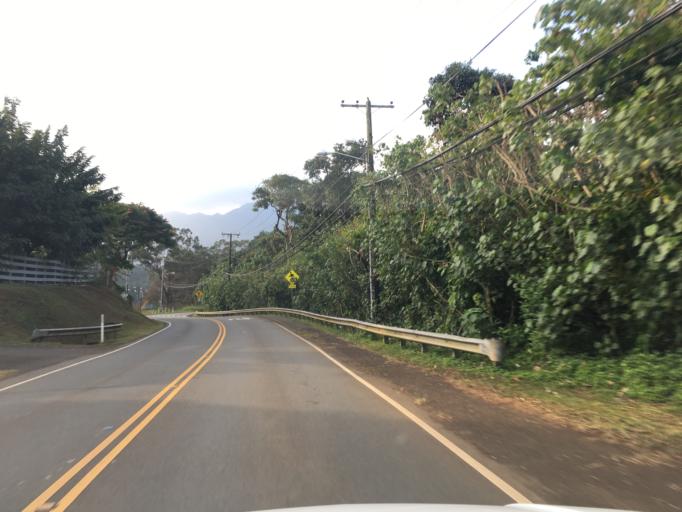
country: US
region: Hawaii
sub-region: Honolulu County
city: Maunawili
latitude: 21.3738
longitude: -157.7639
